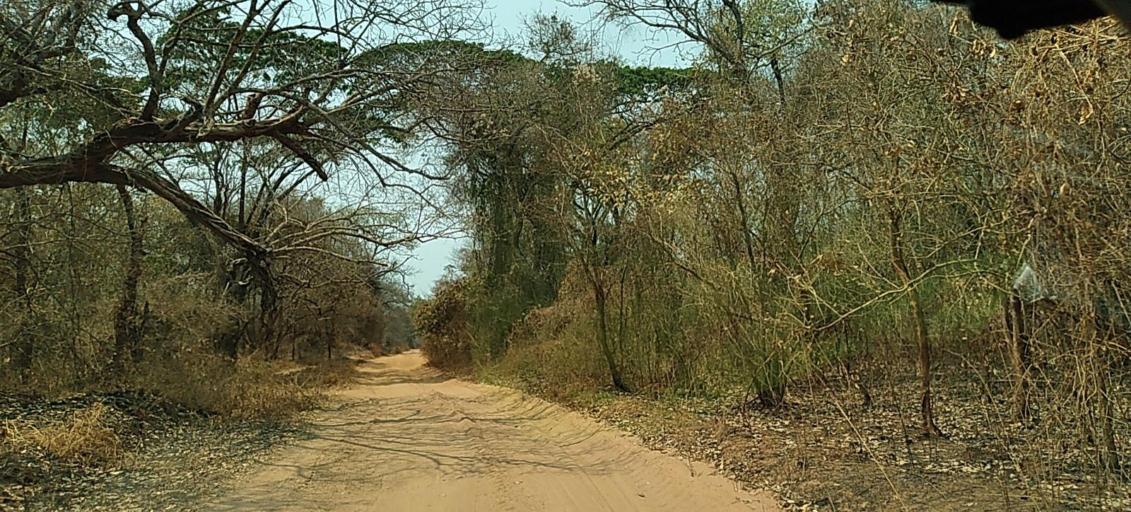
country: ZM
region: North-Western
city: Kabompo
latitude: -13.7018
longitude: 24.3184
